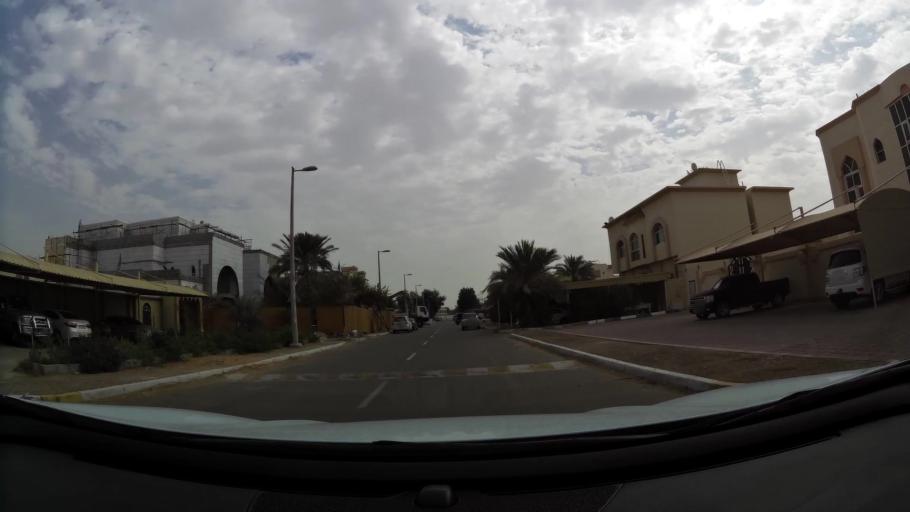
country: AE
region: Abu Dhabi
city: Abu Dhabi
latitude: 24.3152
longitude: 54.6398
